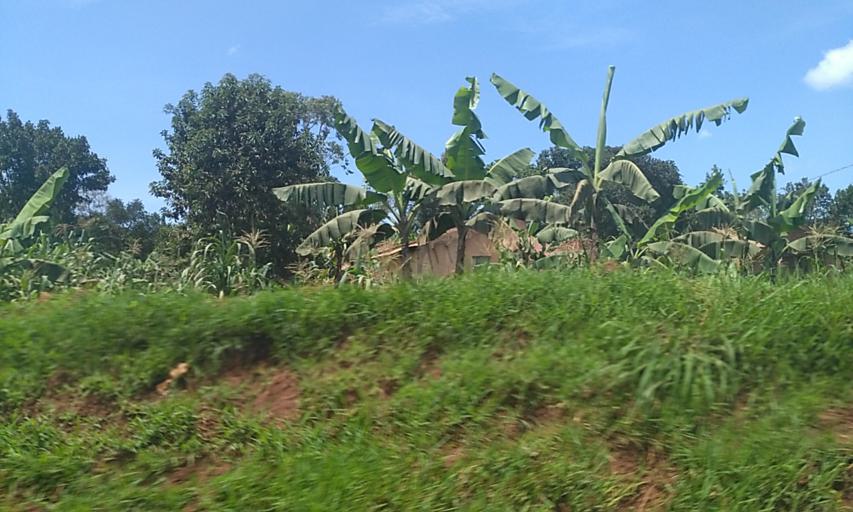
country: UG
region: Central Region
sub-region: Wakiso District
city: Wakiso
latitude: 0.4043
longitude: 32.4893
